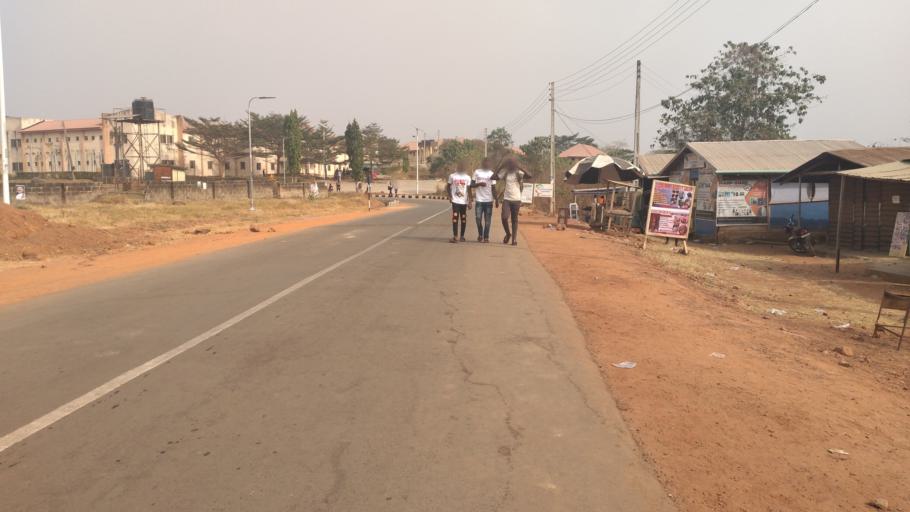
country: NG
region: Ondo
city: Ilare
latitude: 7.3023
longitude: 5.1419
